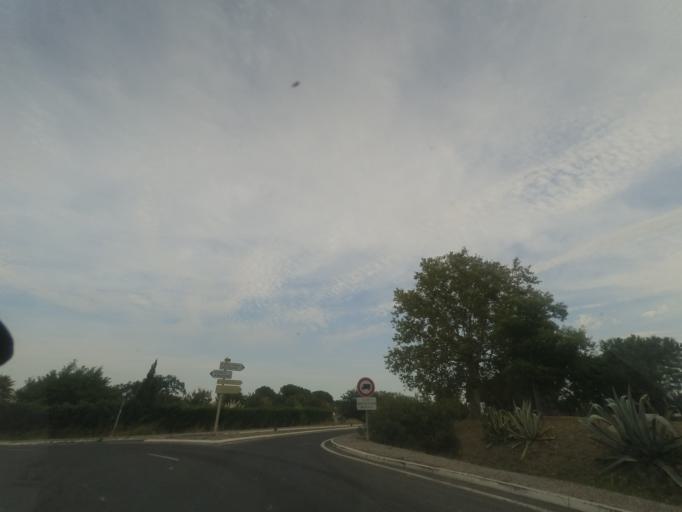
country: FR
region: Languedoc-Roussillon
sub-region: Departement des Pyrenees-Orientales
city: Corneilla-la-Riviere
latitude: 42.6798
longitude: 2.7483
